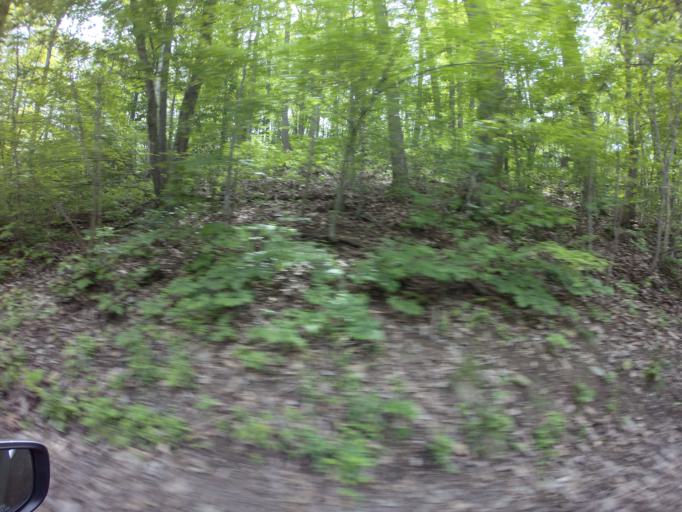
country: US
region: Maryland
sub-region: Carroll County
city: New Windsor
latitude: 39.4826
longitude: -77.0984
